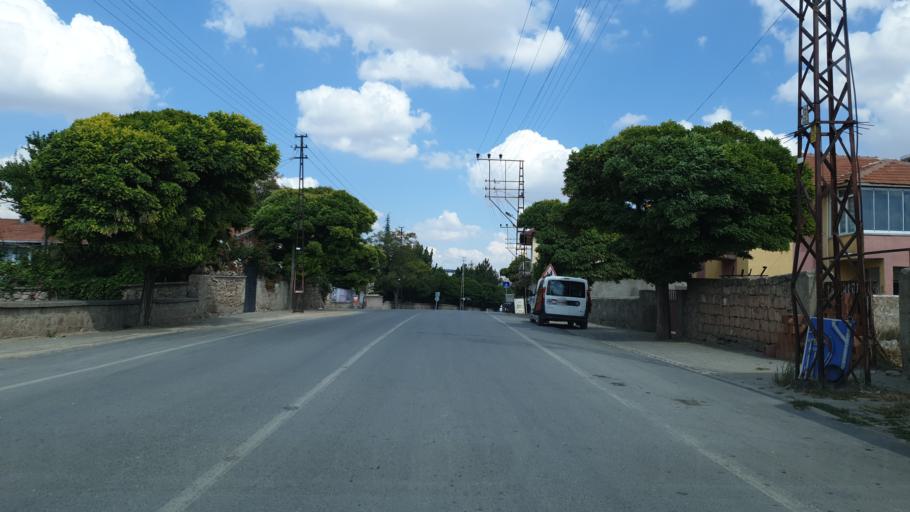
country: TR
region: Kayseri
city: Felahiye
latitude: 39.0902
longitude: 35.5675
